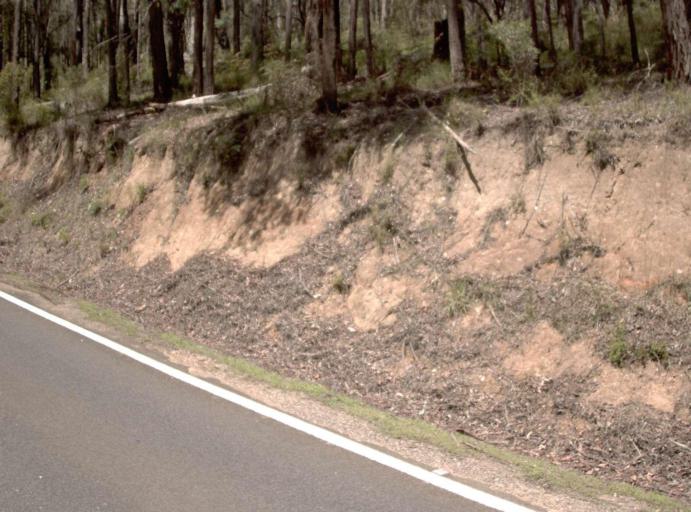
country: AU
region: New South Wales
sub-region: Bombala
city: Bombala
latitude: -37.5944
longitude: 148.9141
